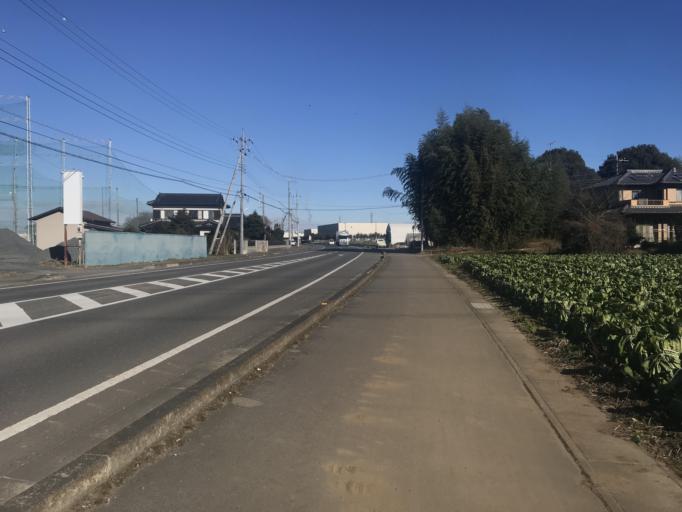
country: JP
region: Ibaraki
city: Yuki
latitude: 36.3202
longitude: 139.8790
